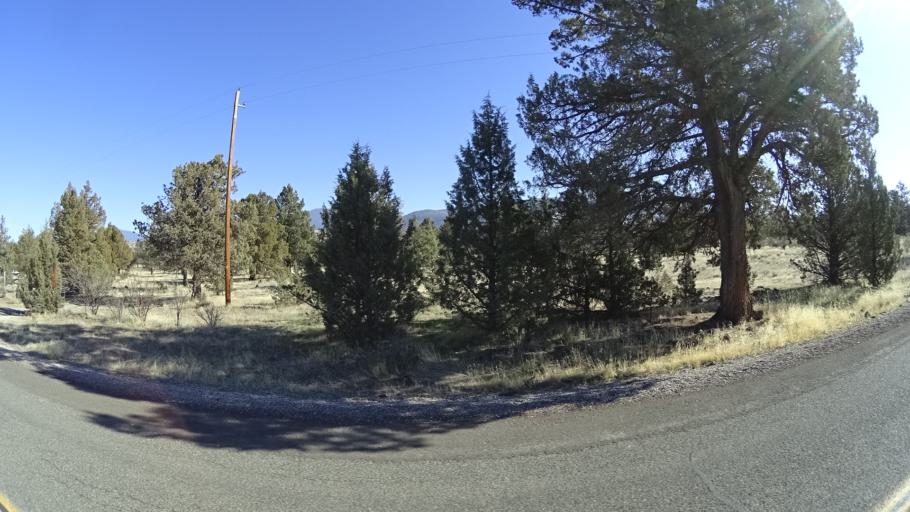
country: US
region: California
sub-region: Siskiyou County
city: Montague
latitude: 41.6515
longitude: -122.3600
